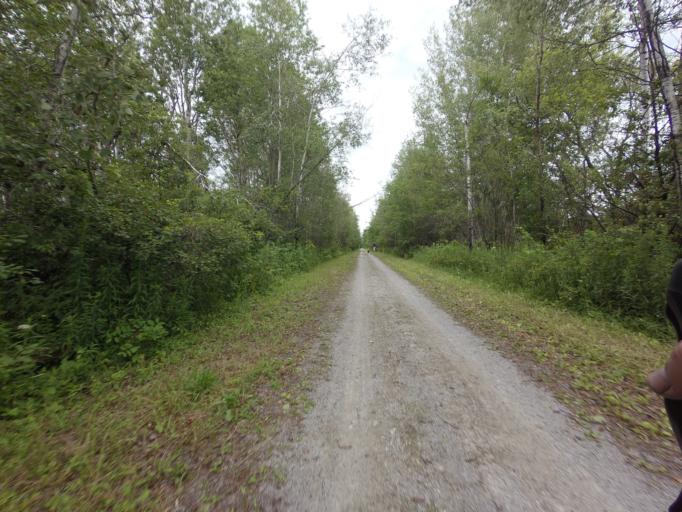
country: CA
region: Ontario
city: Ottawa
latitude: 45.1776
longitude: -75.6187
